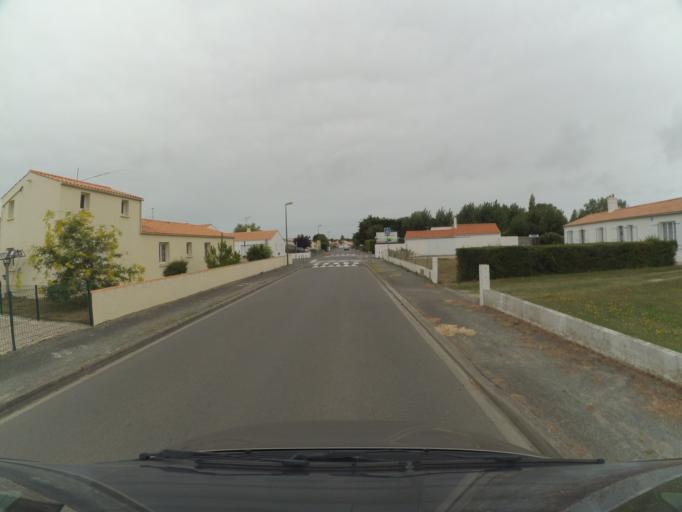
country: FR
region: Pays de la Loire
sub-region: Departement de la Vendee
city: La Barre-de-Monts
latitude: 46.8810
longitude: -2.1108
